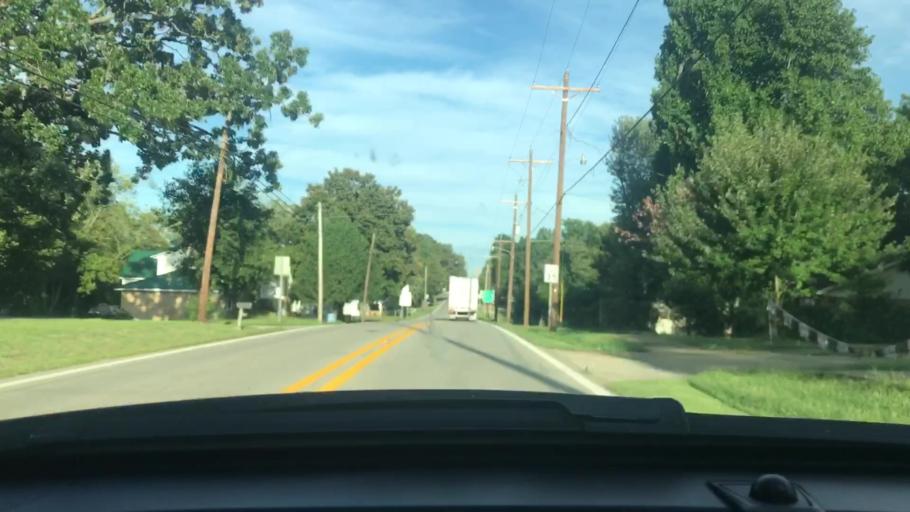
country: US
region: Arkansas
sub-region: Randolph County
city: Pocahontas
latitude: 36.2039
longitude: -91.1858
